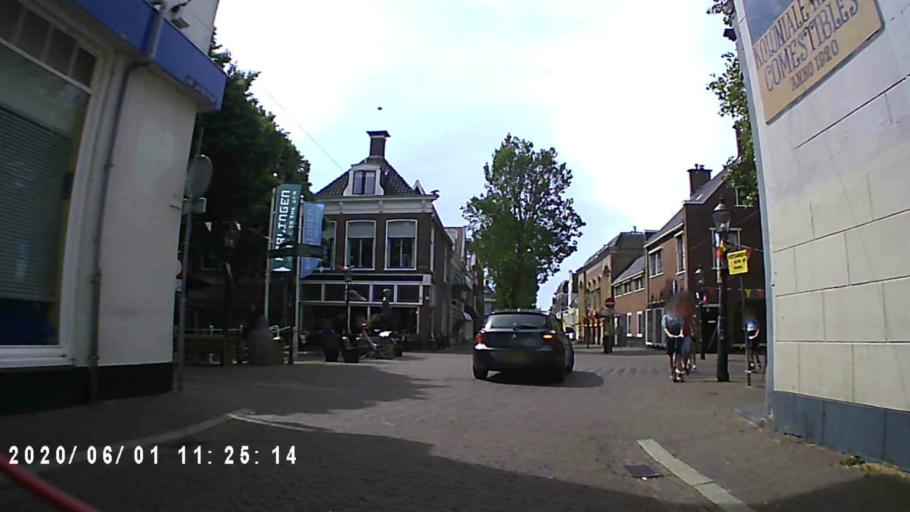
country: NL
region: Friesland
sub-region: Gemeente Harlingen
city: Harlingen
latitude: 53.1748
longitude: 5.4198
